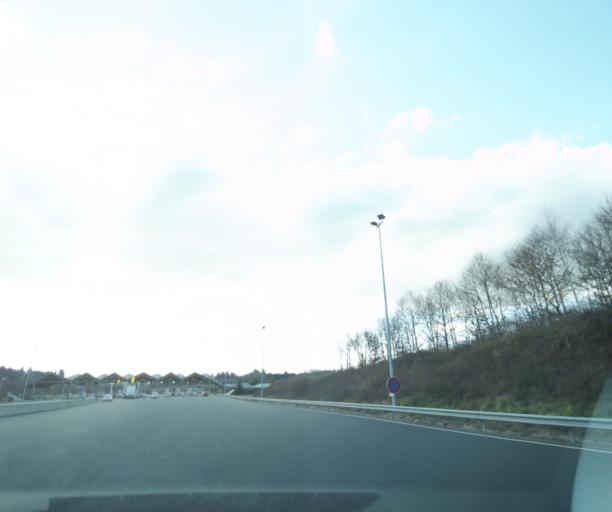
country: FR
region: Limousin
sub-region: Departement de la Correze
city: Saint-Mexant
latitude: 45.2853
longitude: 1.6191
